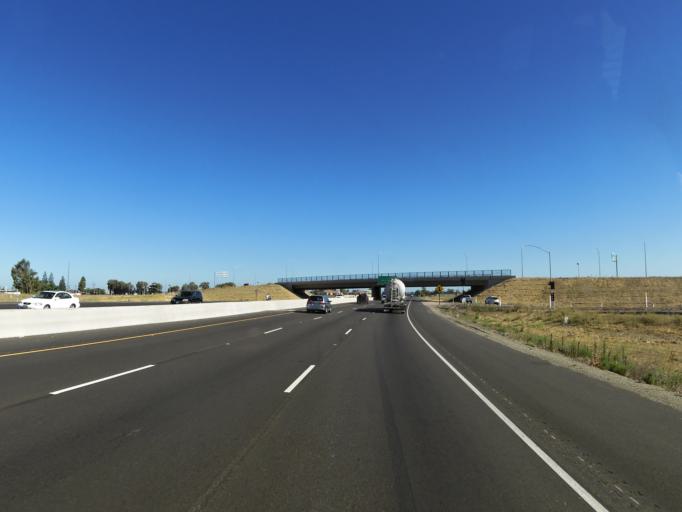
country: US
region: California
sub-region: San Joaquin County
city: Kennedy
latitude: 37.9319
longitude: -121.2336
